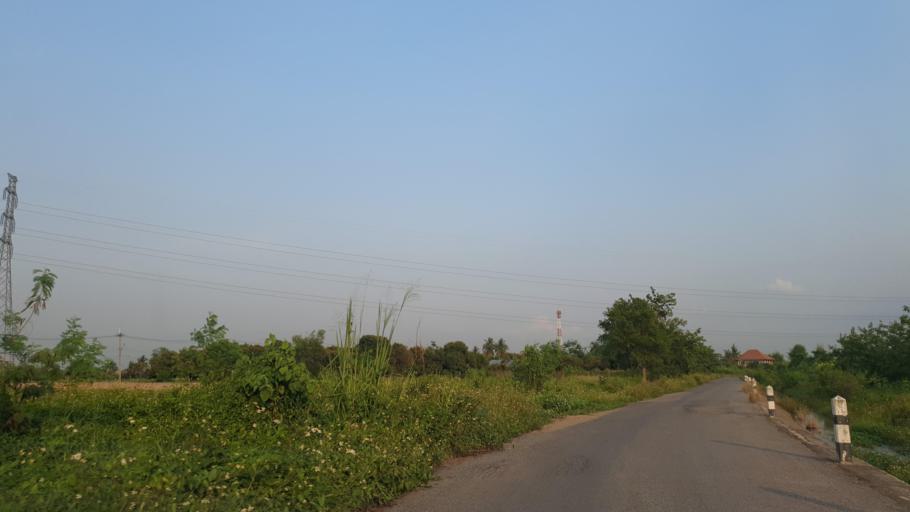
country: TH
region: Chiang Mai
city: Hang Dong
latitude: 18.6578
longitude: 98.9339
